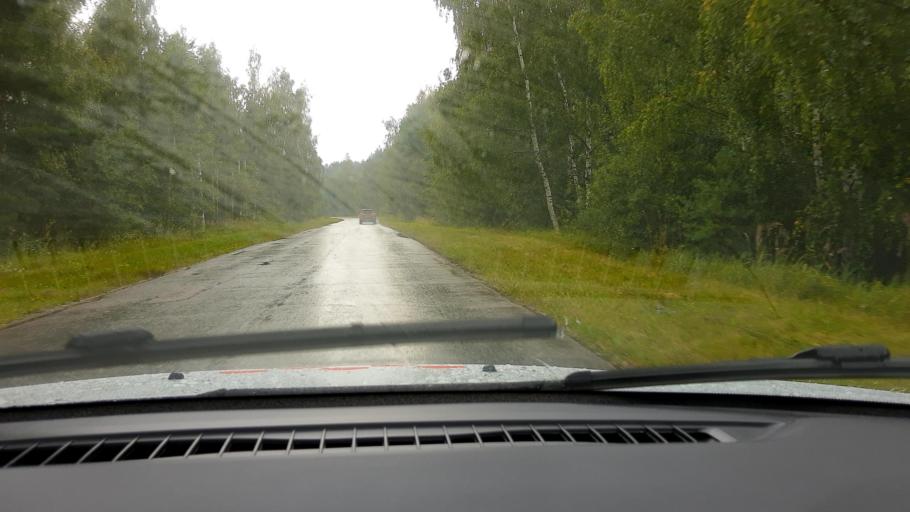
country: RU
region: Nizjnij Novgorod
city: Surovatikha
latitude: 55.9521
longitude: 43.9592
